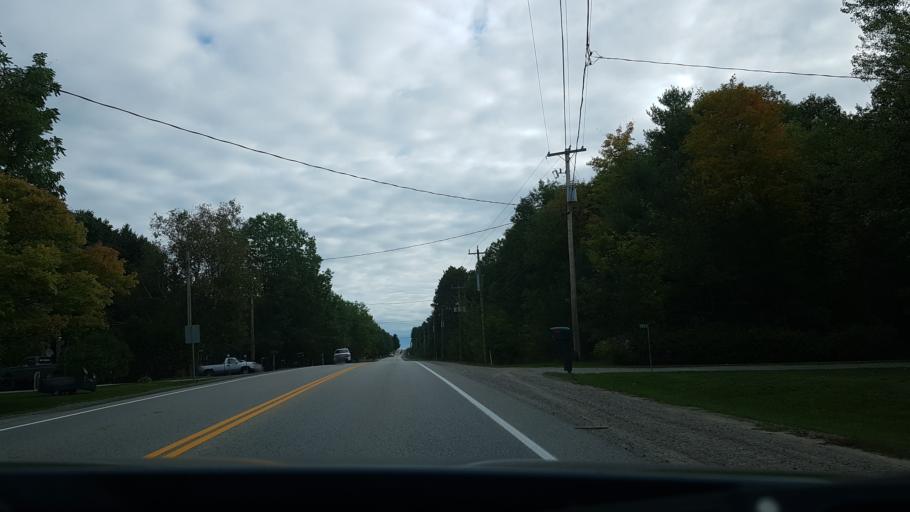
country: CA
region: Ontario
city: Barrie
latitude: 44.4882
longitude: -79.8171
